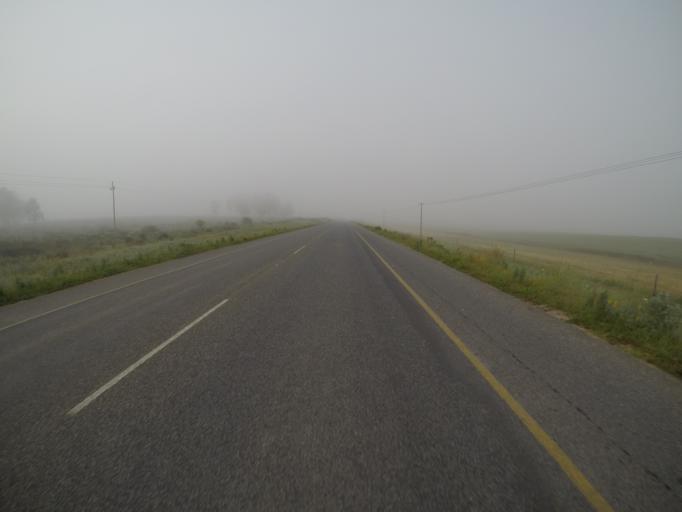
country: ZA
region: Western Cape
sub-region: City of Cape Town
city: Kraaifontein
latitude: -33.6832
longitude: 18.7054
